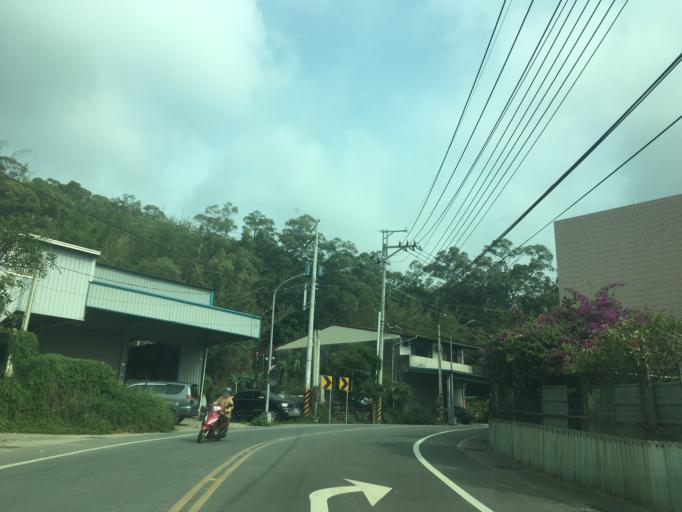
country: TW
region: Taiwan
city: Fengyuan
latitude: 24.2385
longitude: 120.7345
